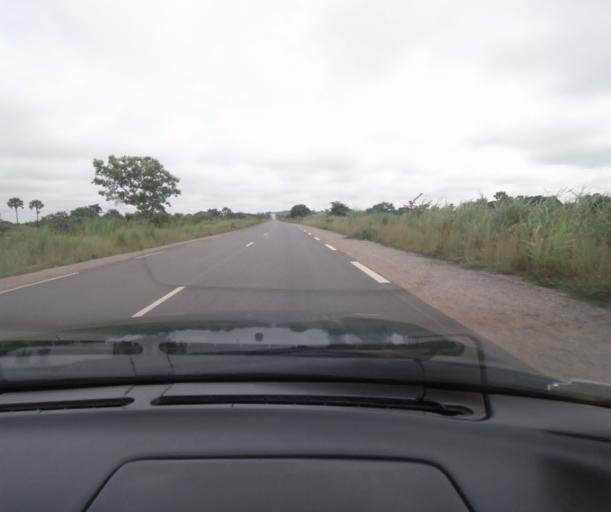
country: CM
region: Centre
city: Saa
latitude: 4.3897
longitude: 11.2546
